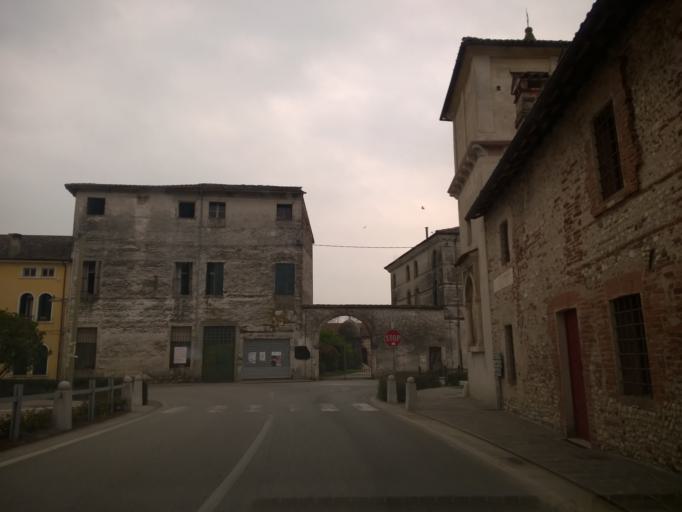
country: IT
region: Veneto
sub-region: Provincia di Vicenza
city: Poianella
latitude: 45.6408
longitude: 11.6085
